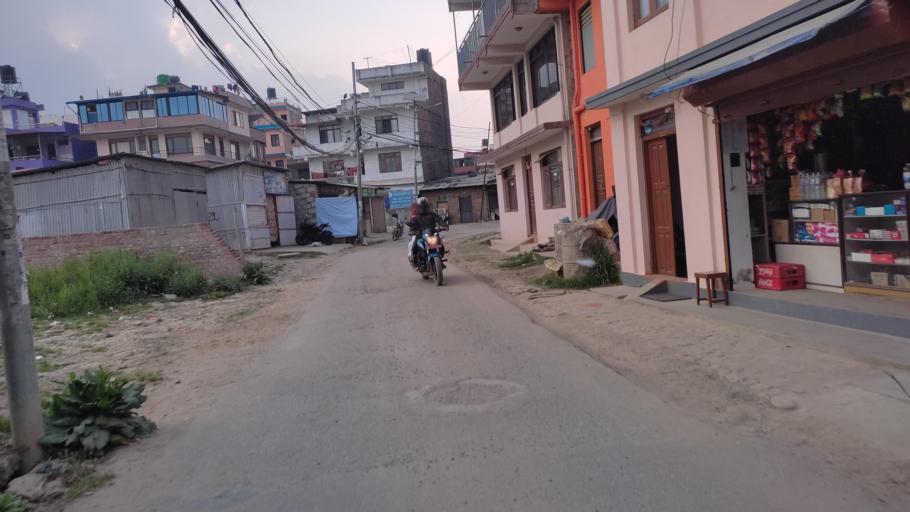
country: NP
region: Central Region
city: Kirtipur
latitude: 27.6682
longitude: 85.2741
